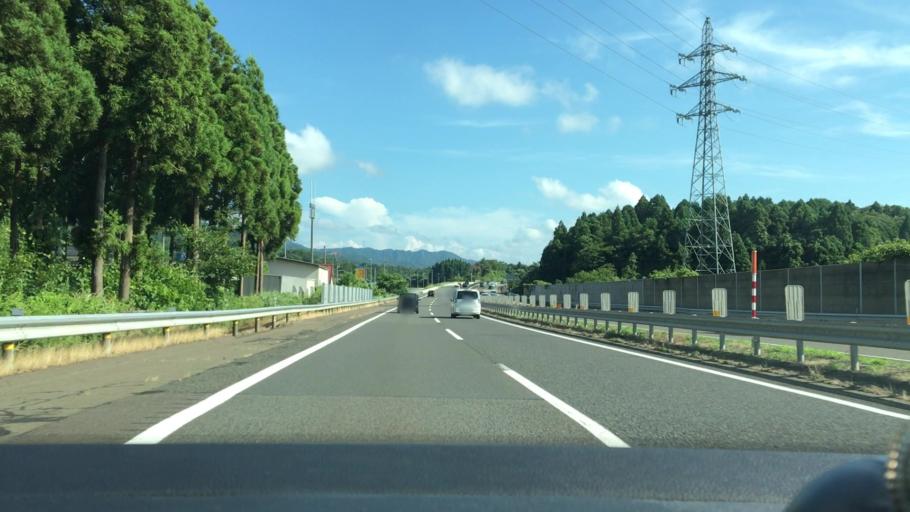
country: JP
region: Fukui
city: Maruoka
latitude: 36.2526
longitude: 136.2842
